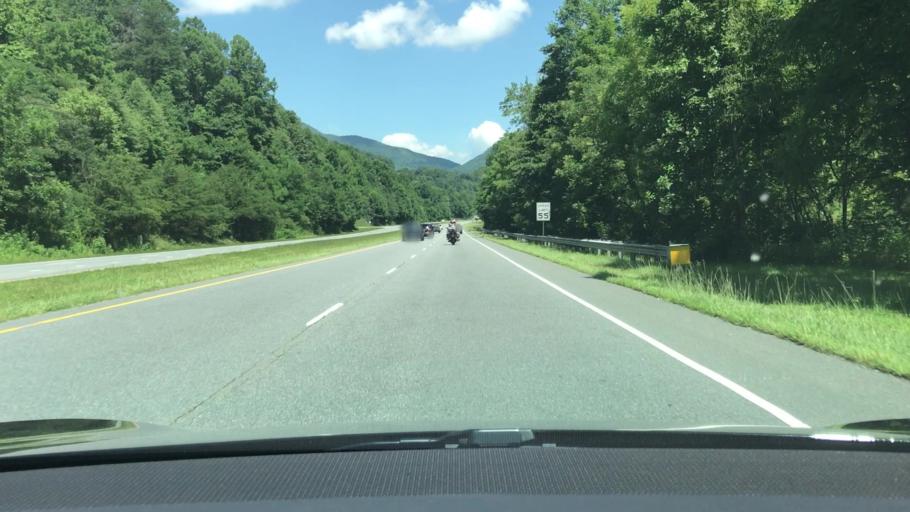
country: US
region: North Carolina
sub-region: Jackson County
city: Sylva
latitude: 35.3095
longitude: -83.2593
